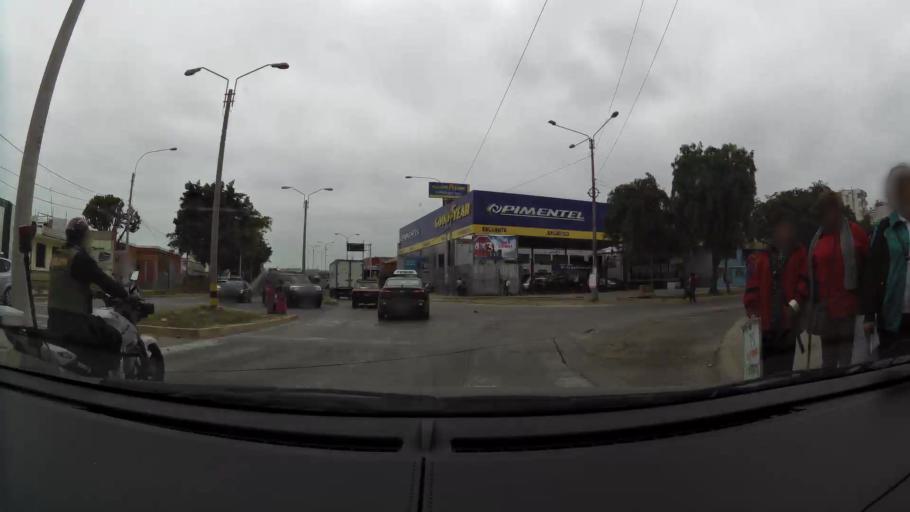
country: PE
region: La Libertad
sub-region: Provincia de Trujillo
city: Trujillo
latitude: -8.1062
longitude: -79.0328
